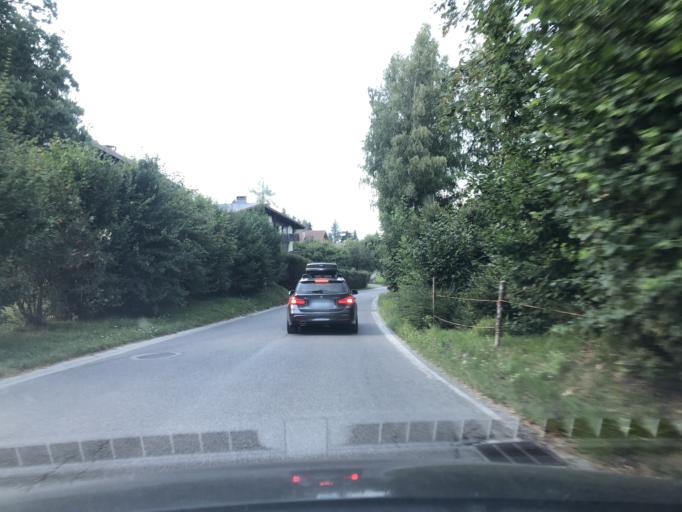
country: FR
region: Rhone-Alpes
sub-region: Departement de la Haute-Savoie
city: Combloux
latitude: 45.8914
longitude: 6.6353
